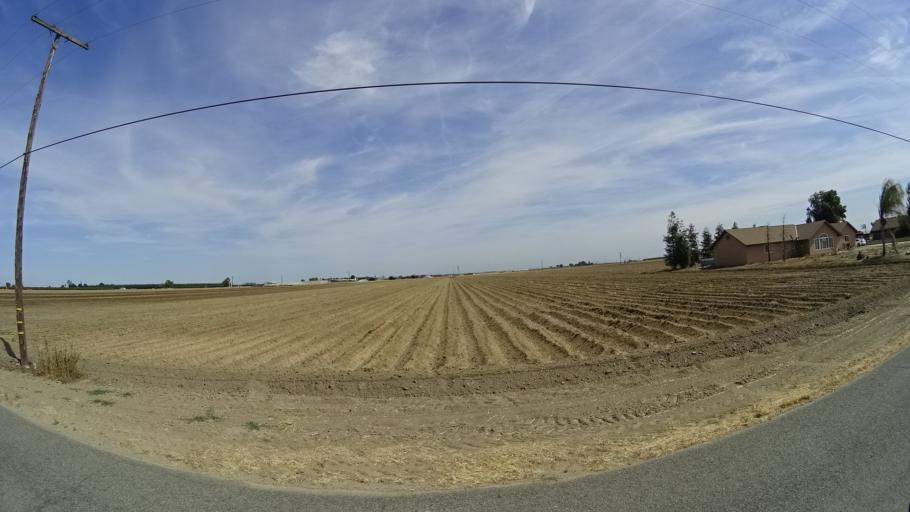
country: US
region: California
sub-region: Kings County
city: Hanford
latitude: 36.3573
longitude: -119.5716
